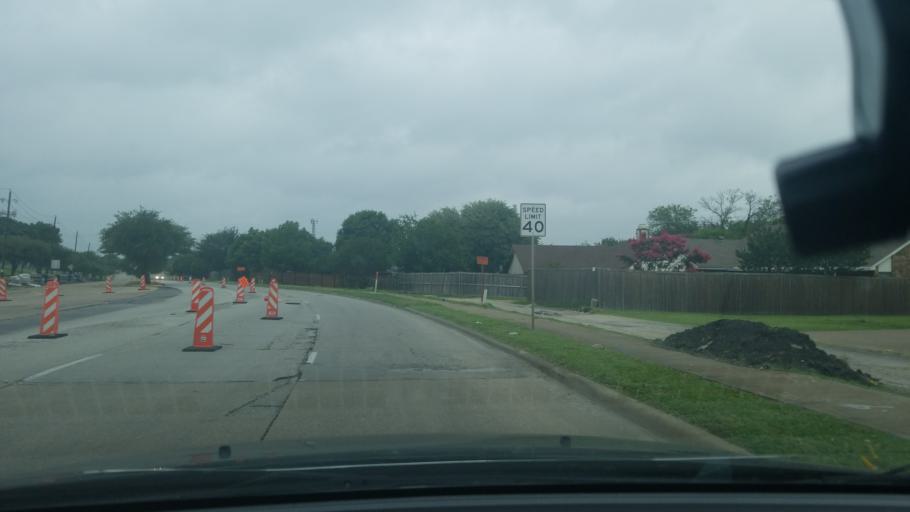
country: US
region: Texas
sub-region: Dallas County
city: Mesquite
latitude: 32.7814
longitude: -96.6459
